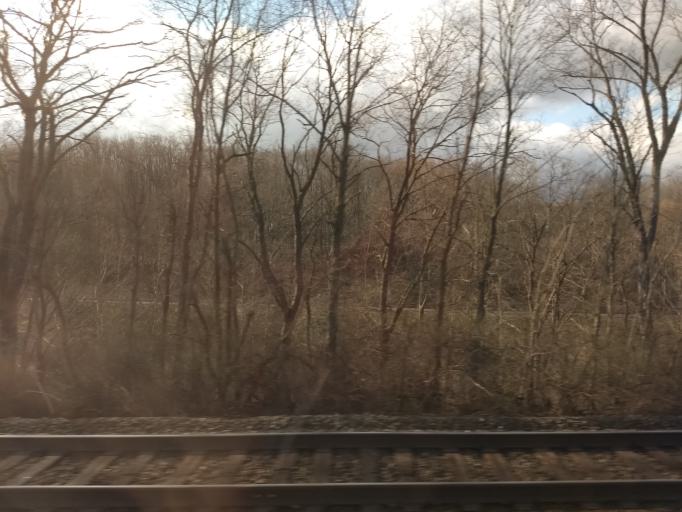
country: US
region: Pennsylvania
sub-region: Cambria County
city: Portage
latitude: 40.3802
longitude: -78.7355
